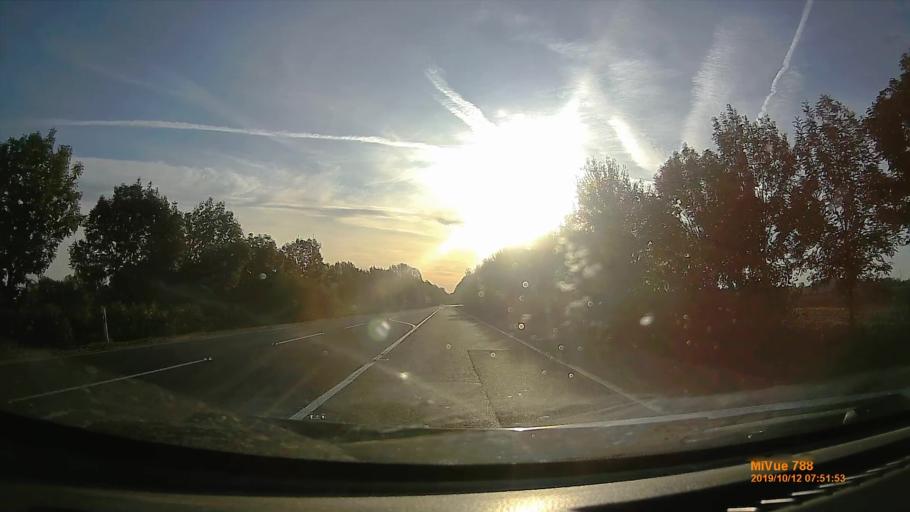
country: HU
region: Hajdu-Bihar
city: Biharkeresztes
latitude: 47.1393
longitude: 21.7320
